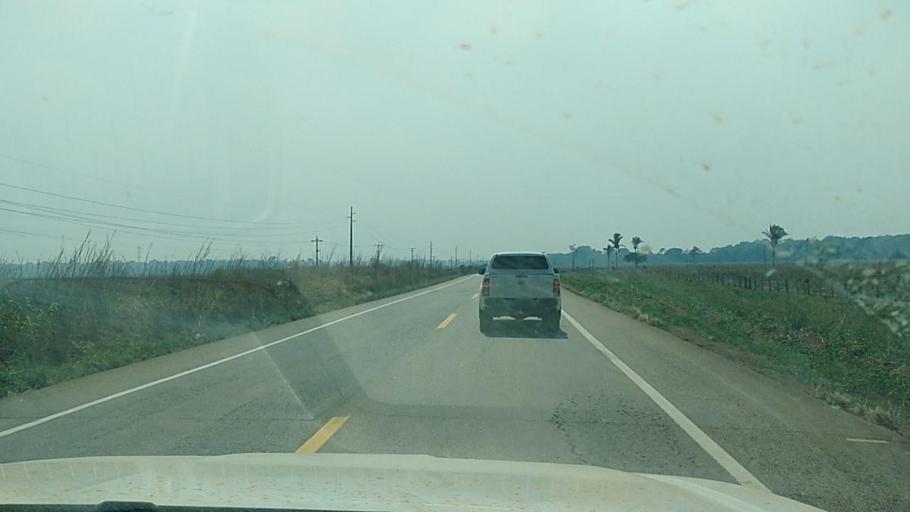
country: BR
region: Rondonia
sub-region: Porto Velho
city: Porto Velho
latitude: -8.7838
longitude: -63.5621
